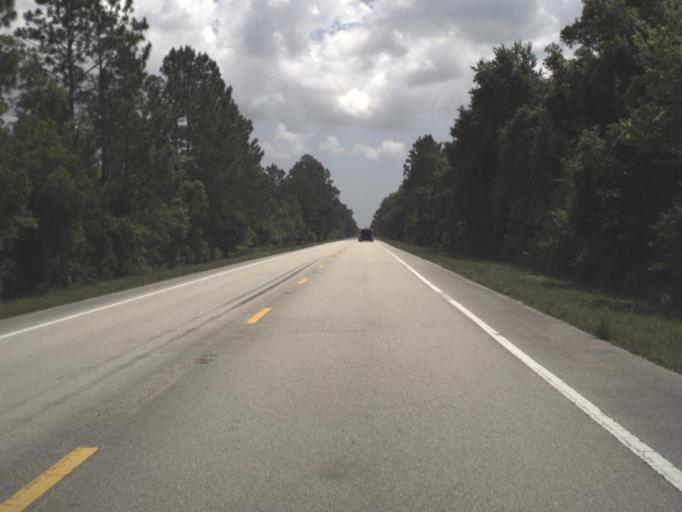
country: US
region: Florida
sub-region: Saint Johns County
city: Saint Augustine Shores
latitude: 29.7332
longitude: -81.3825
